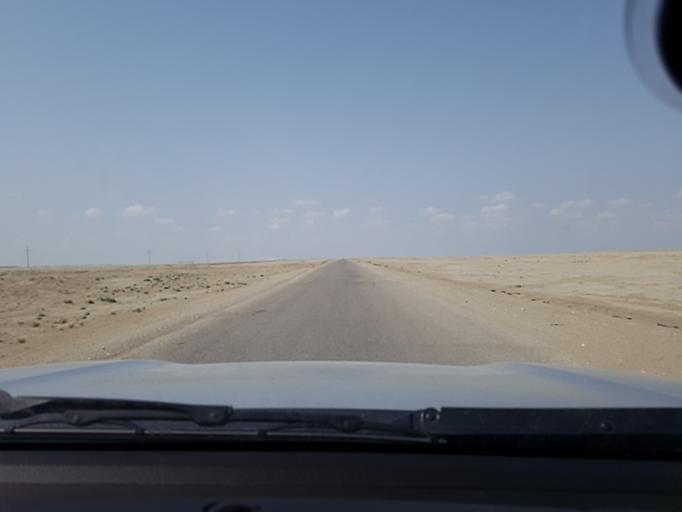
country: TM
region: Balkan
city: Gumdag
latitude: 38.6533
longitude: 54.3879
